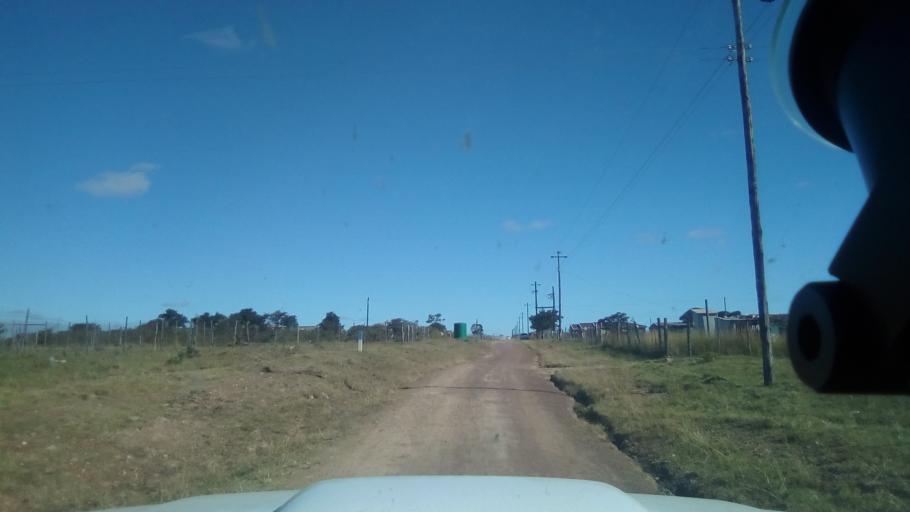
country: ZA
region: Eastern Cape
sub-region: Buffalo City Metropolitan Municipality
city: Bhisho
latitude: -32.7827
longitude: 27.3347
